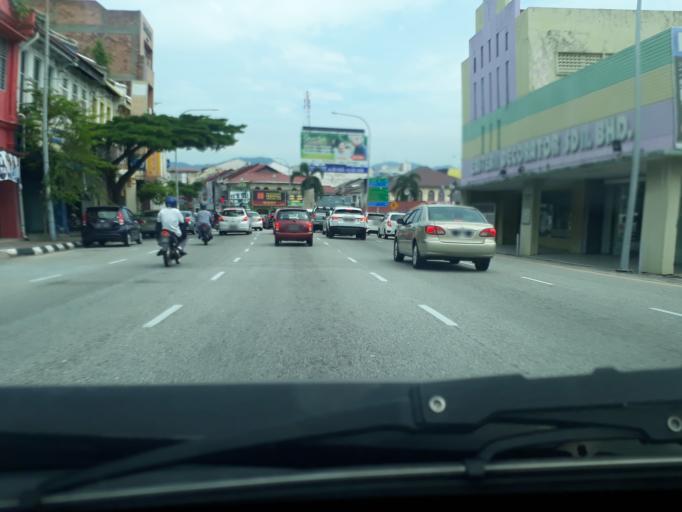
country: MY
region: Perak
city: Ipoh
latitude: 4.5927
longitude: 101.0856
